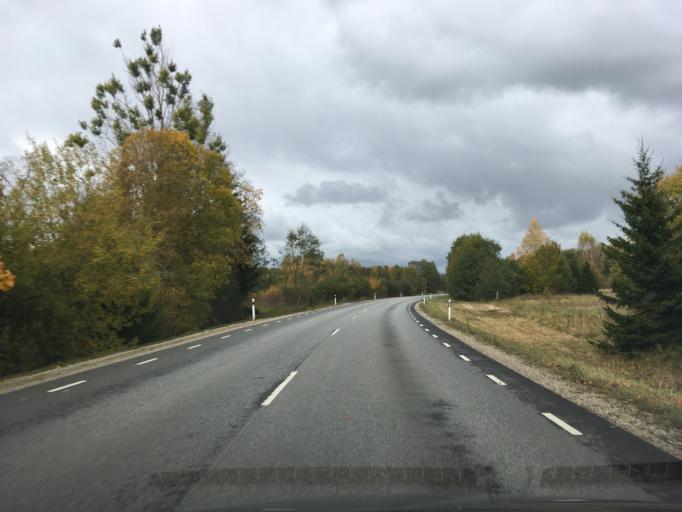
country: EE
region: Harju
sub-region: Anija vald
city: Kehra
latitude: 59.3000
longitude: 25.3613
